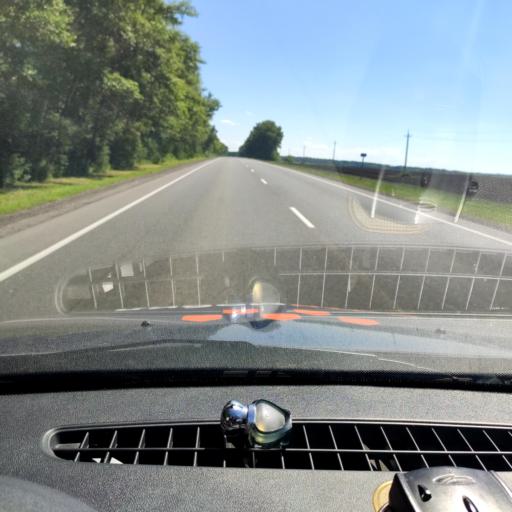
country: RU
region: Orjol
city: Pokrovskoye
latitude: 52.5246
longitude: 37.0421
